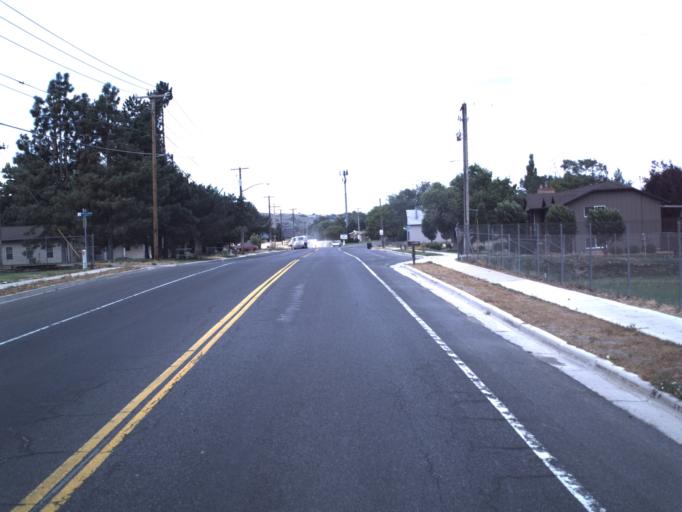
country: US
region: Utah
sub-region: Davis County
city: South Weber
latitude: 41.1325
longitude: -111.9341
